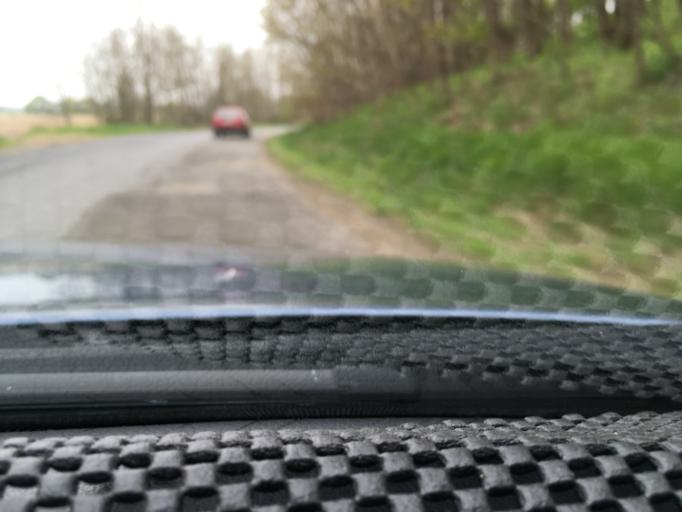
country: HU
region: Hajdu-Bihar
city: Nyiradony
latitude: 47.6896
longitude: 21.9326
